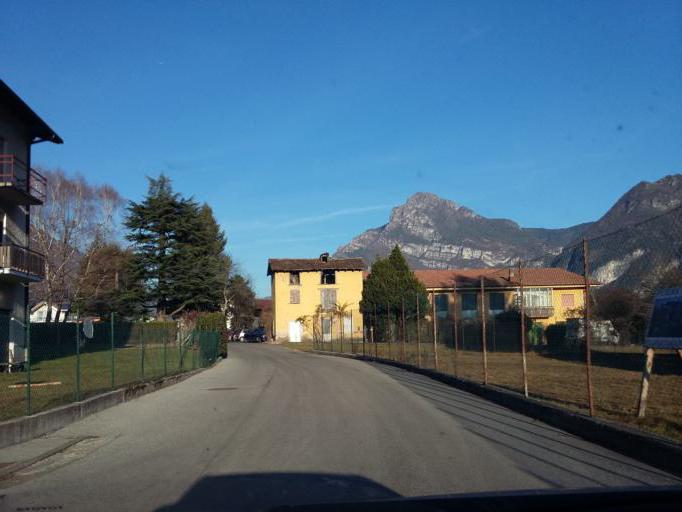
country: IT
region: Trentino-Alto Adige
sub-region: Provincia di Trento
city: Lodrone-Darzo
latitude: 45.8295
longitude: 10.5402
